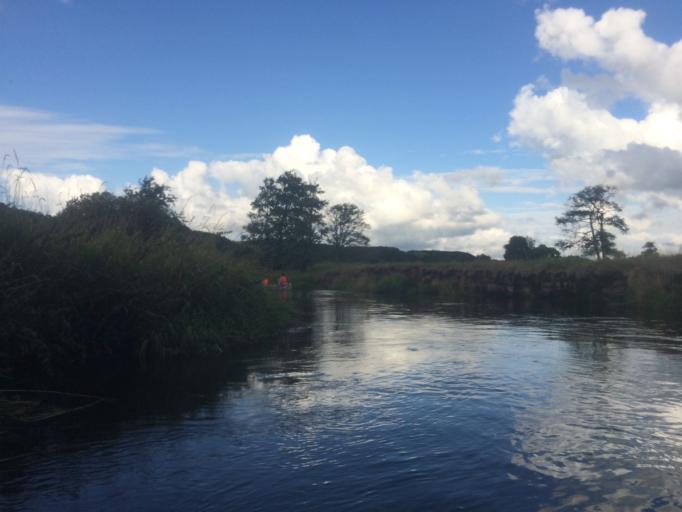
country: DK
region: South Denmark
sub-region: Vejle Kommune
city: Egtved
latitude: 55.6643
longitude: 9.3341
